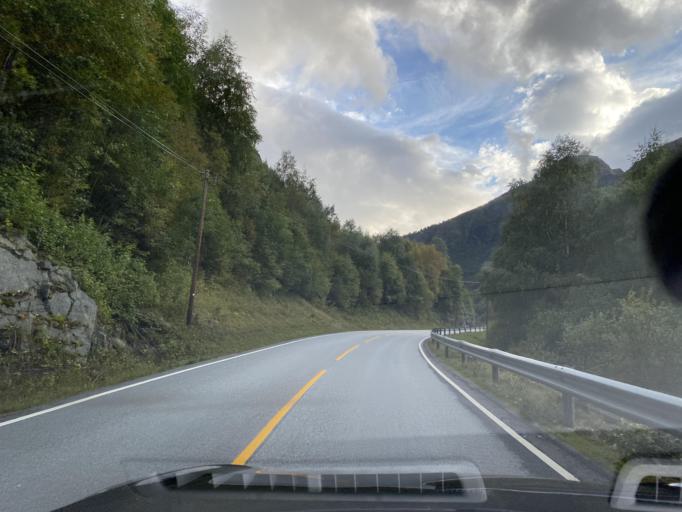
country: NO
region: Oppland
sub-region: Lom
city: Fossbergom
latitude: 61.8043
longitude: 8.4541
